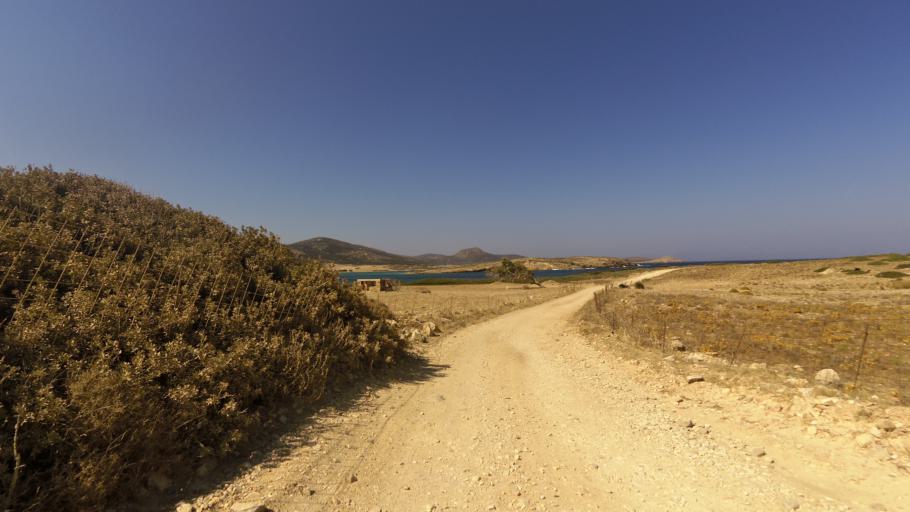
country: GR
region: South Aegean
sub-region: Nomos Kykladon
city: Antiparos
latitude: 36.9780
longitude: 25.0258
